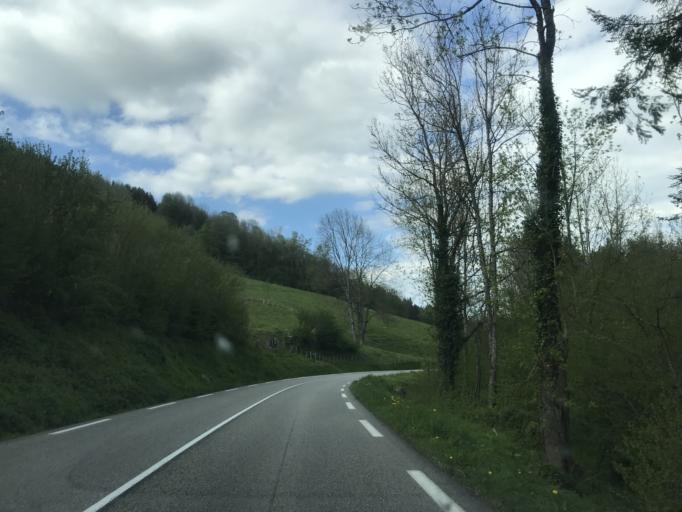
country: FR
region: Rhone-Alpes
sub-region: Departement de l'Isere
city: La Buisse
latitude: 45.3358
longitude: 5.6596
